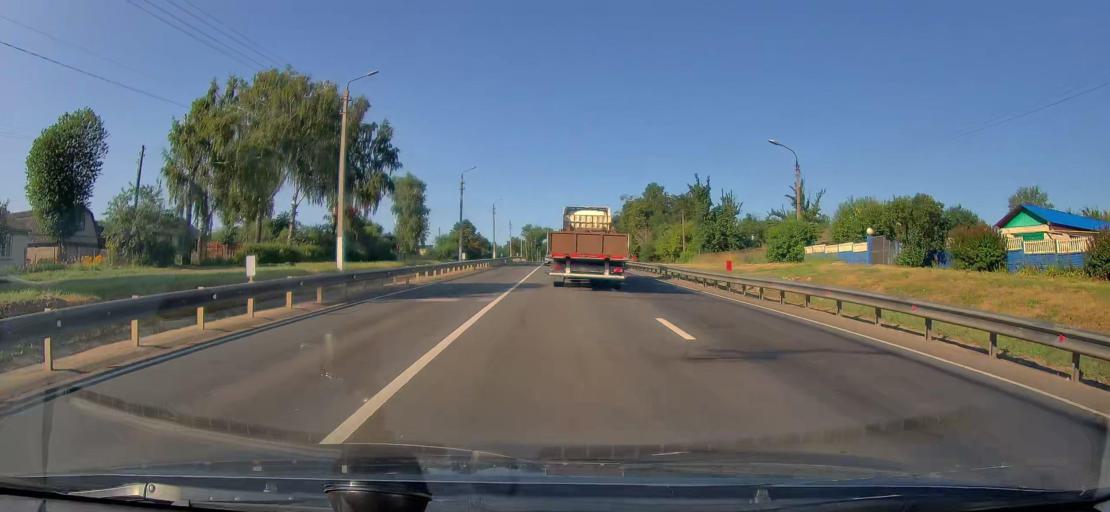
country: RU
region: Orjol
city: Mtsensk
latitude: 53.1846
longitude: 36.4145
